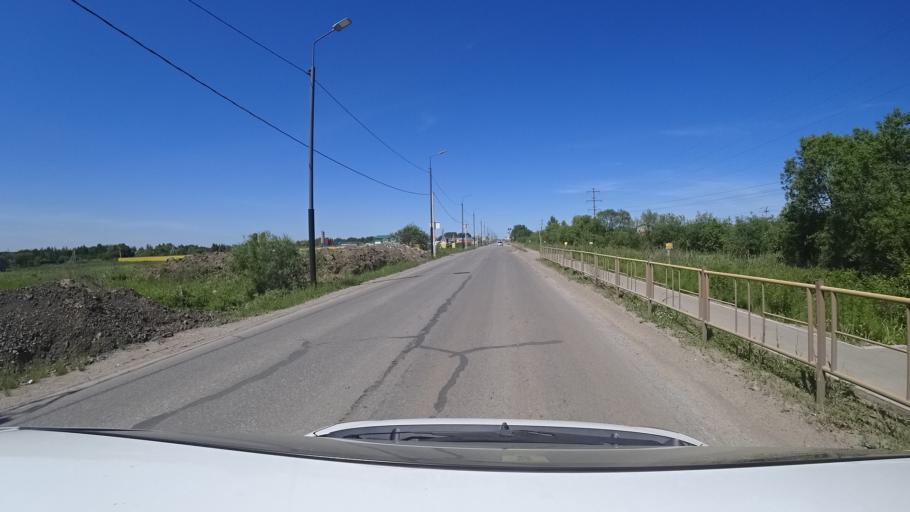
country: RU
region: Khabarovsk Krai
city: Topolevo
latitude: 48.4889
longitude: 135.1837
